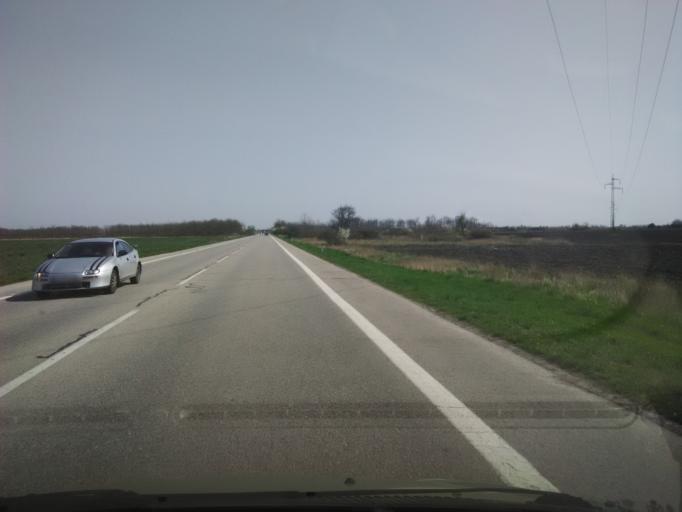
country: SK
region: Nitriansky
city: Sellye
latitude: 48.1398
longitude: 17.9976
